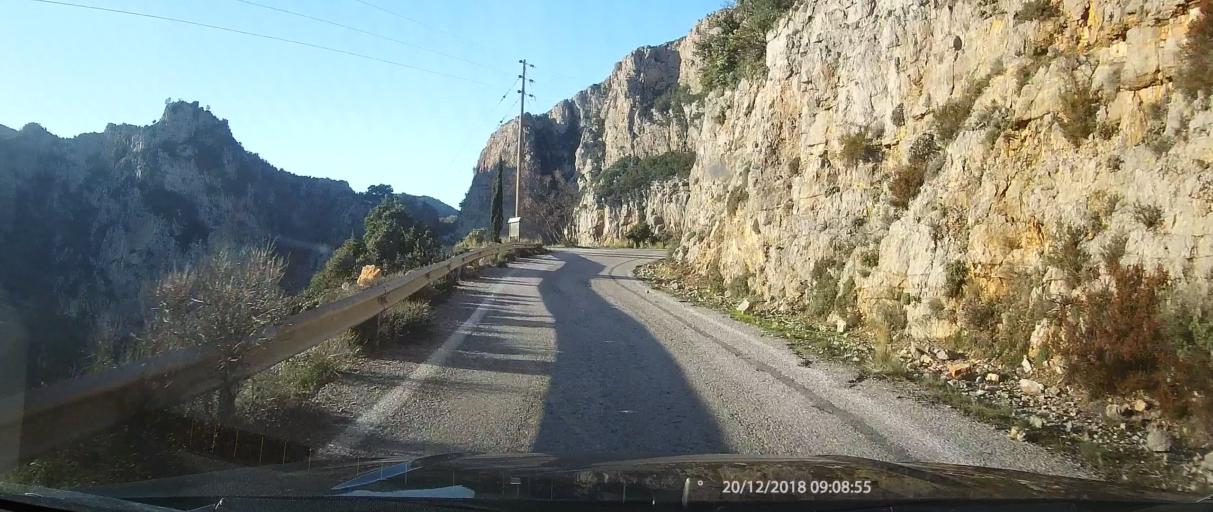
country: GR
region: Peloponnese
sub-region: Nomos Lakonias
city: Sykea
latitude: 36.9202
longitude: 23.0053
